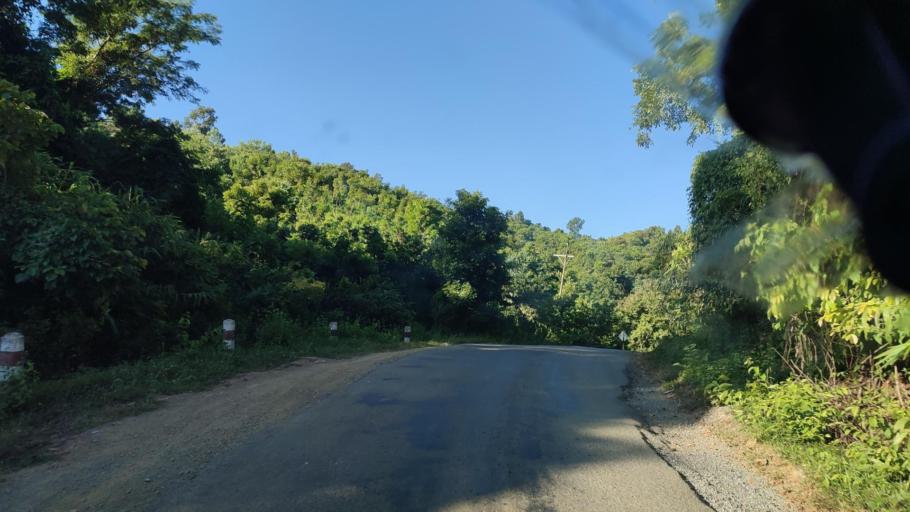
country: MM
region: Rakhine
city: Sittwe
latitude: 19.9157
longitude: 93.8030
